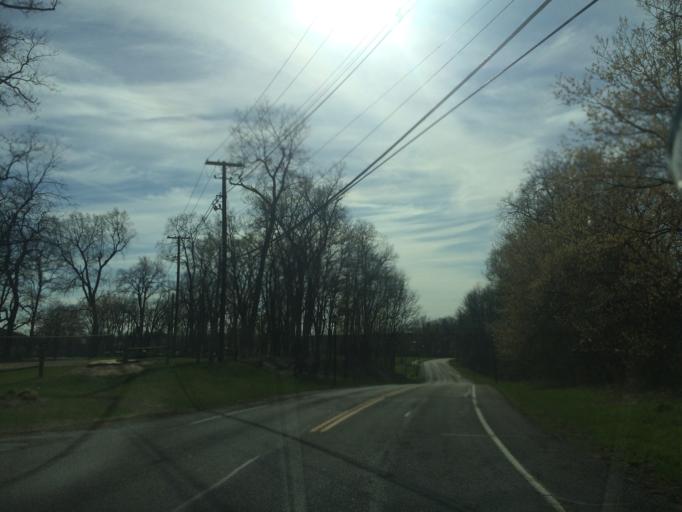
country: US
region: New York
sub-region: Monroe County
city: Fairport
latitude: 43.1025
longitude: -77.4554
